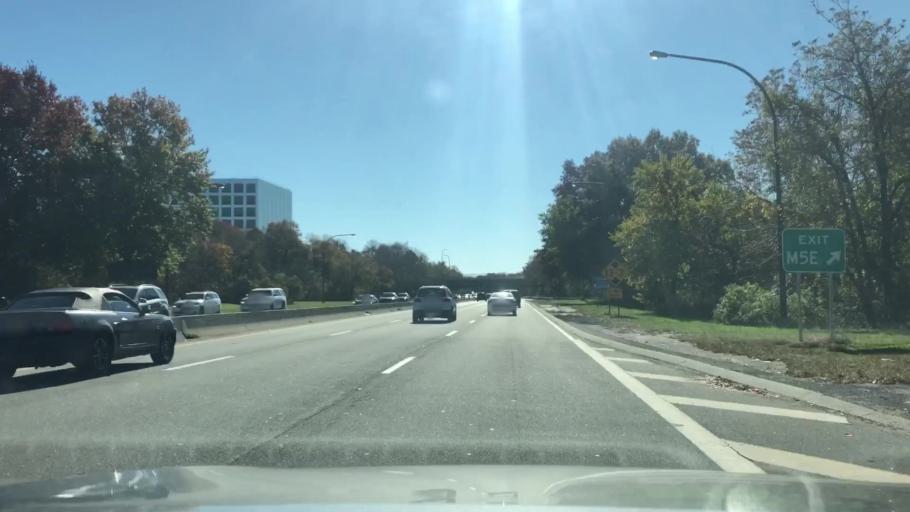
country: US
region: New York
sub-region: Nassau County
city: East Garden City
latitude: 40.7214
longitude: -73.5807
